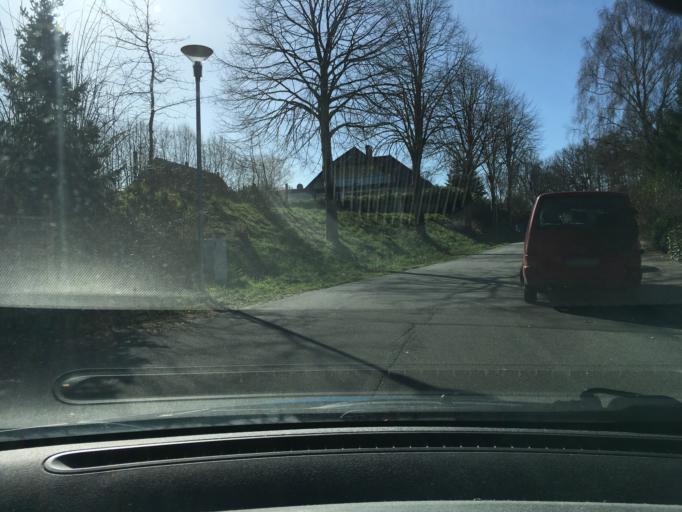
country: DE
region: Schleswig-Holstein
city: Fahrdorf
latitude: 54.5031
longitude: 9.5996
